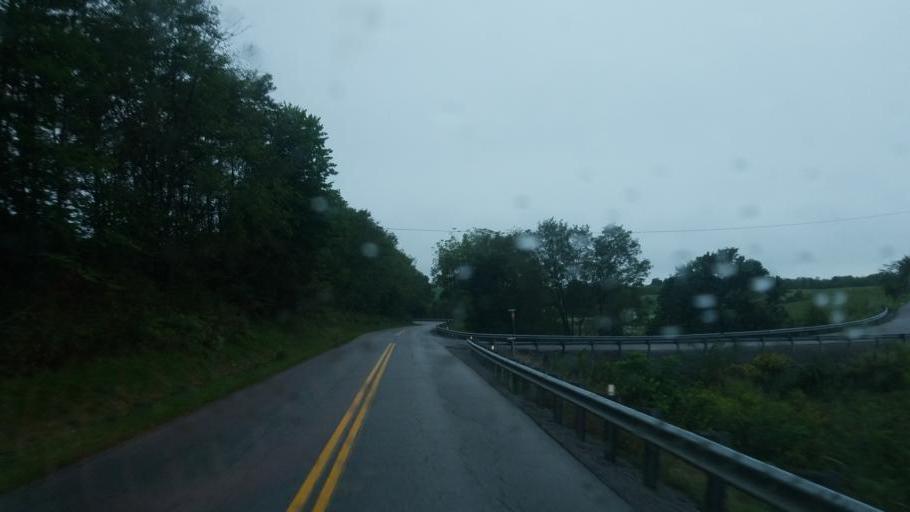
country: US
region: Kentucky
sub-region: Fleming County
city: Flemingsburg
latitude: 38.4139
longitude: -83.6891
